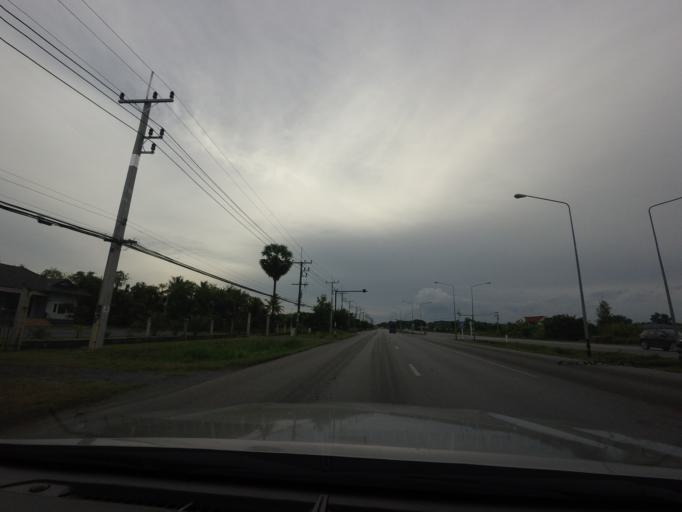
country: TH
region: Nakhon Si Thammarat
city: Chian Yai
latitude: 8.0873
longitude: 100.1415
